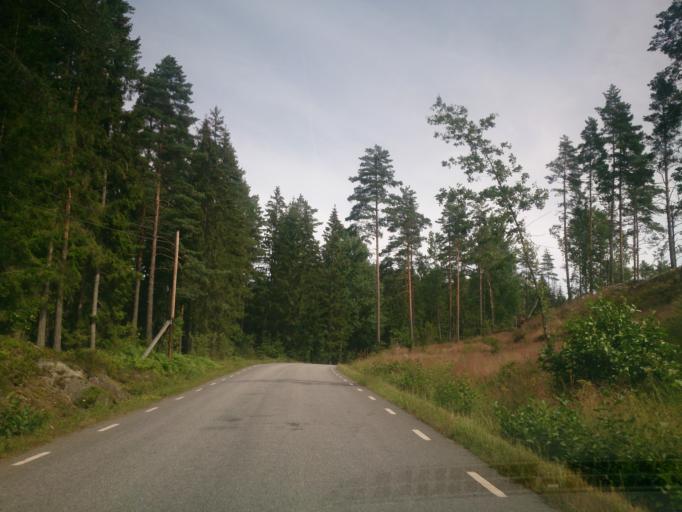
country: SE
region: OEstergoetland
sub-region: Valdemarsviks Kommun
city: Gusum
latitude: 58.3126
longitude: 16.3623
